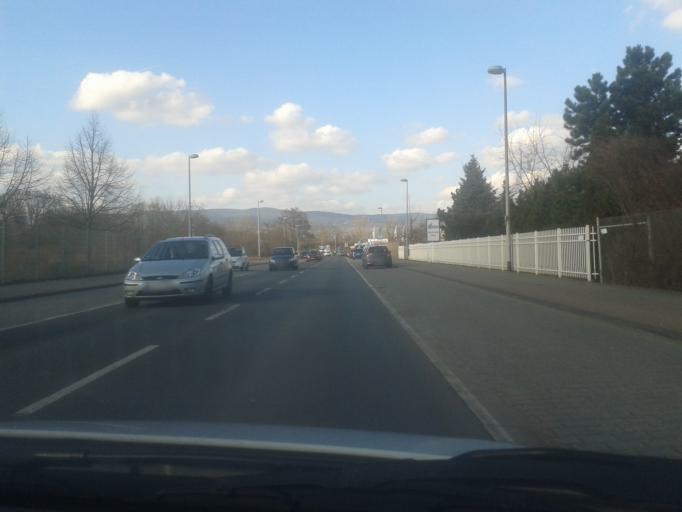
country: DE
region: Rheinland-Pfalz
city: Ingelheim am Rhein
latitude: 49.9827
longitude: 8.0515
